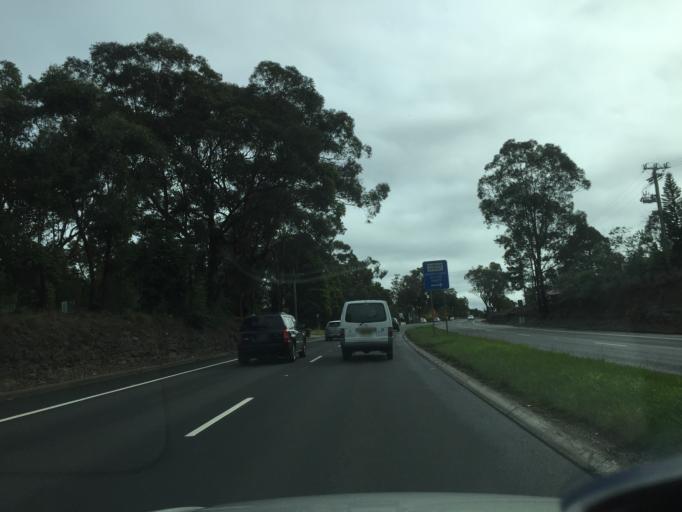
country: AU
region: New South Wales
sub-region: Blue Mountains Municipality
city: Glenbrook
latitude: -33.7596
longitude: 150.6127
